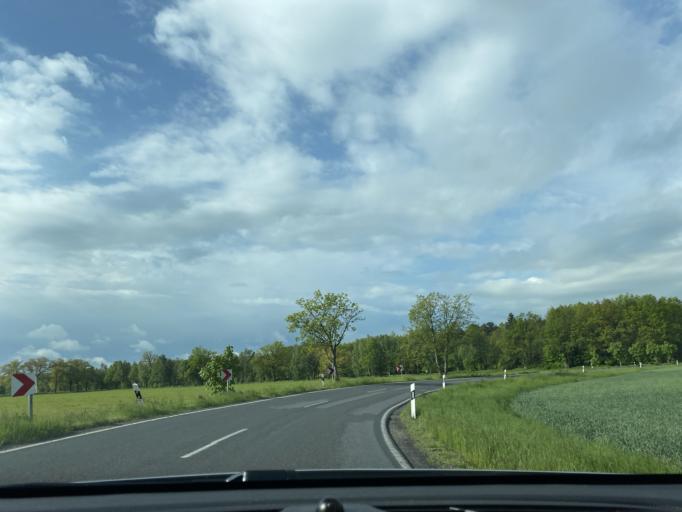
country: DE
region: Saxony
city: Rothenburg
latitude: 51.3181
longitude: 14.9407
